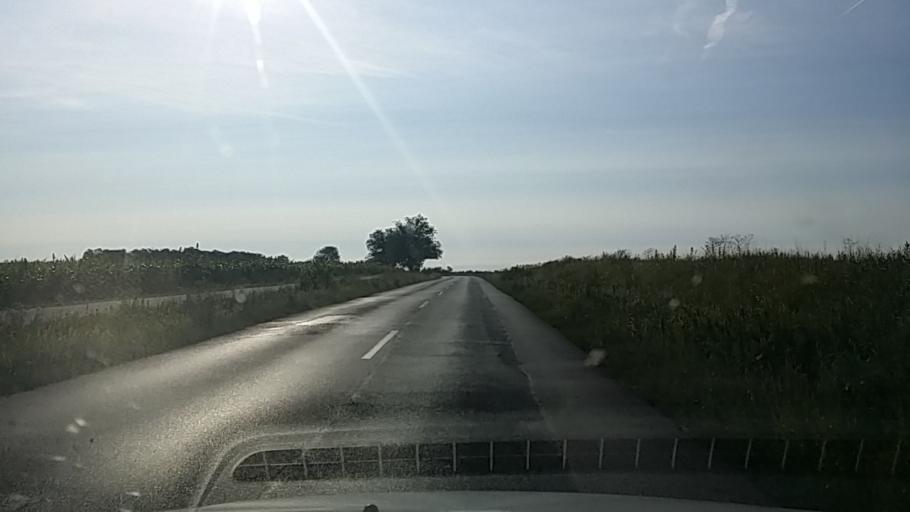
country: HU
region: Gyor-Moson-Sopron
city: Fertod
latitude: 47.6183
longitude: 16.8095
